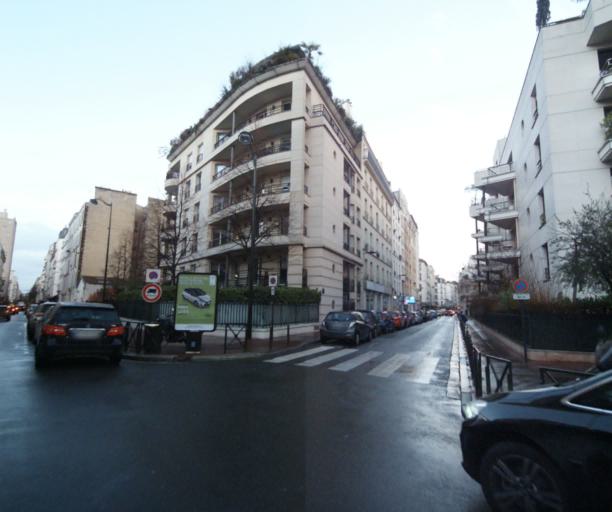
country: FR
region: Ile-de-France
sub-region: Departement des Hauts-de-Seine
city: Levallois-Perret
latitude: 48.8890
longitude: 2.2905
